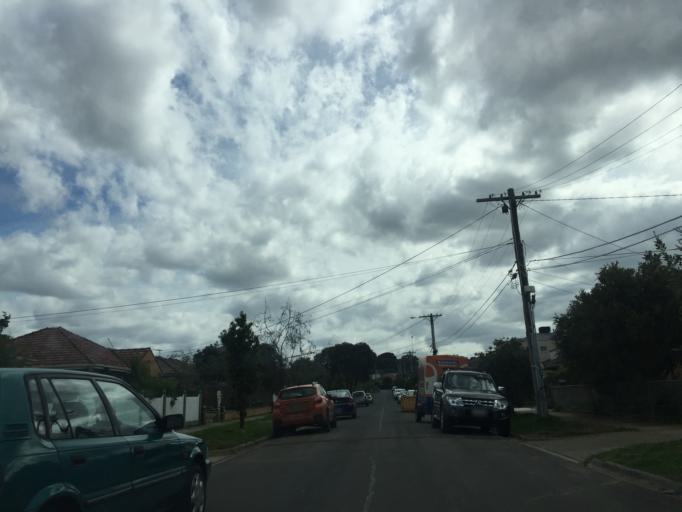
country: AU
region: Victoria
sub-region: Darebin
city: Preston
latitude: -37.7476
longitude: 145.0162
